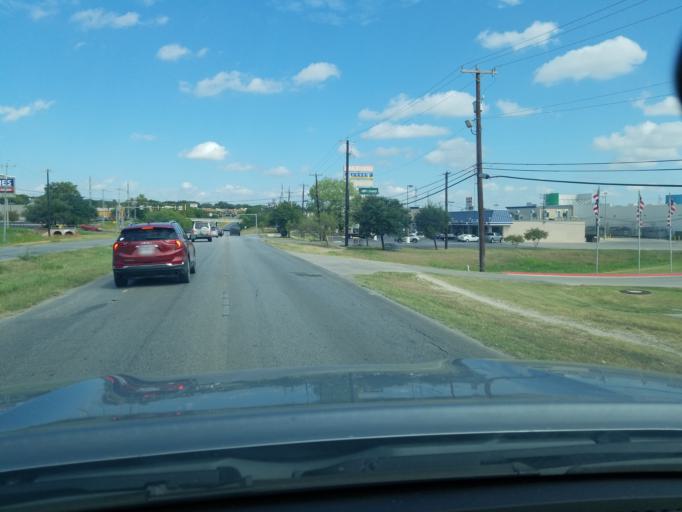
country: US
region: Texas
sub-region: Bexar County
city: Terrell Hills
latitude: 29.4912
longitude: -98.4318
